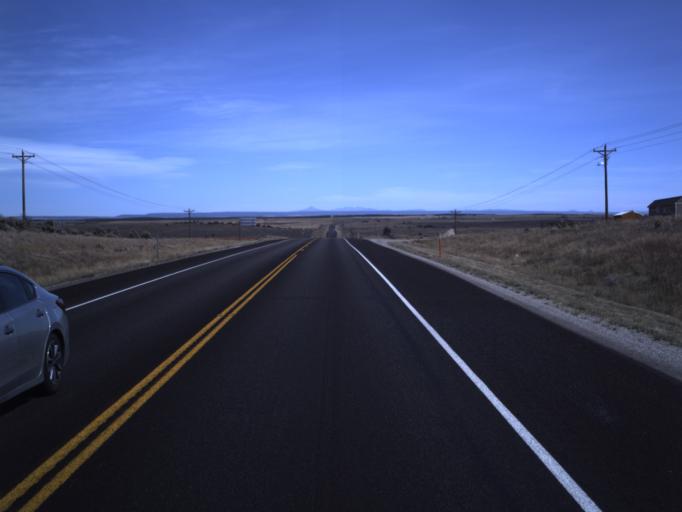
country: US
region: Utah
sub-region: San Juan County
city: Monticello
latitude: 37.8728
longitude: -109.2939
